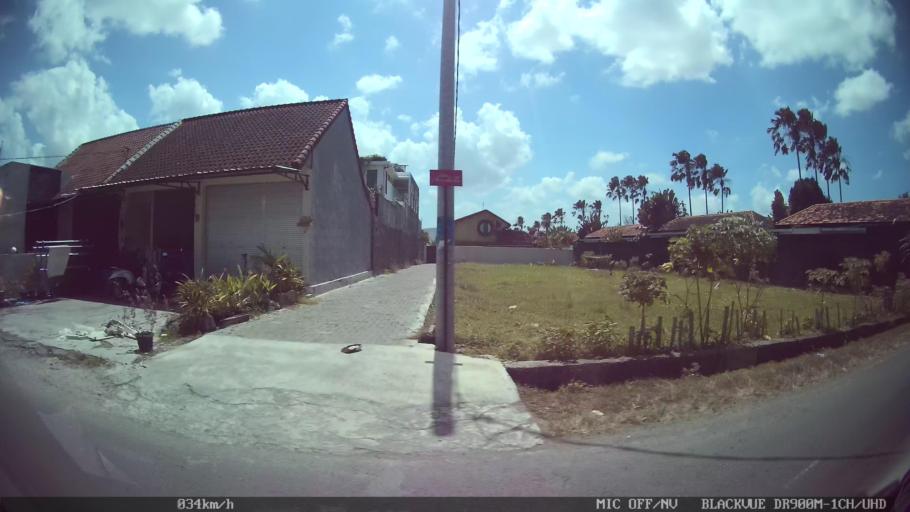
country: ID
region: Bali
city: Banjar Gunungpande
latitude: -8.6661
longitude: 115.1582
